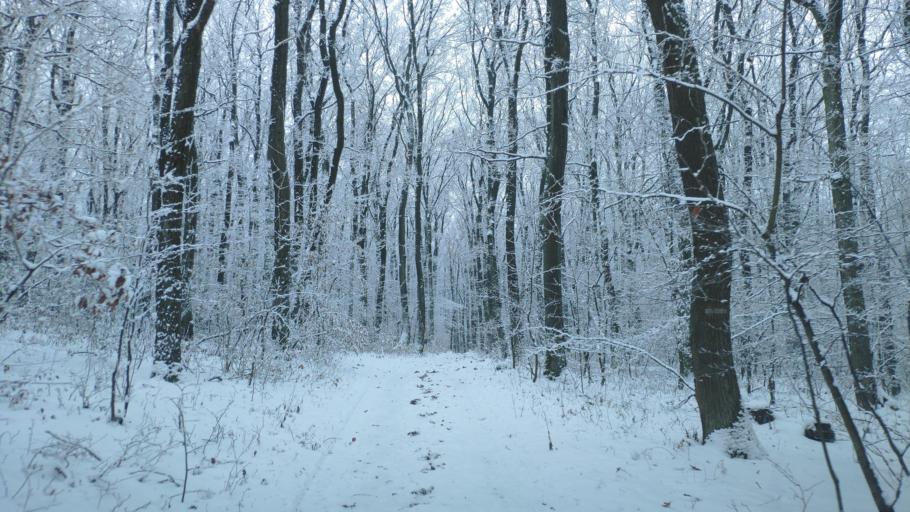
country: SK
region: Kosicky
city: Kosice
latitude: 48.6598
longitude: 21.1833
